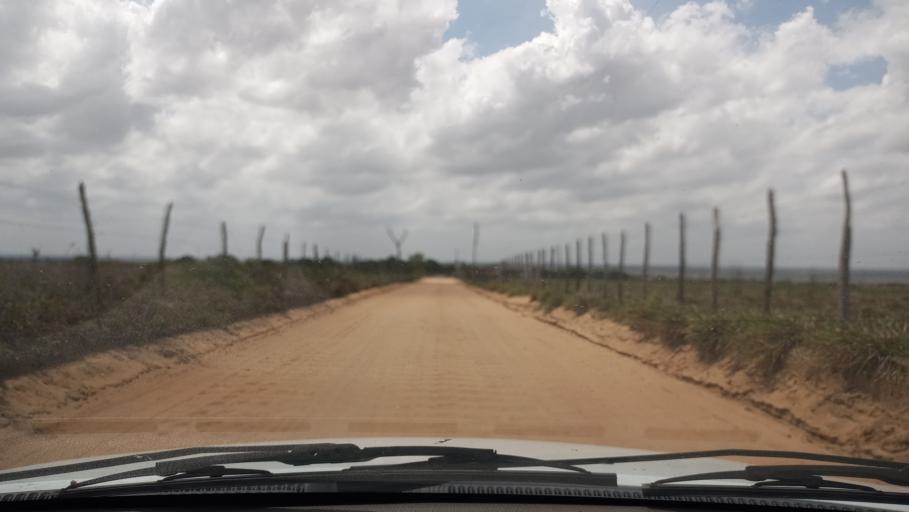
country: BR
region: Rio Grande do Norte
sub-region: Montanhas
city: Montanhas
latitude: -6.3625
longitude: -35.3320
